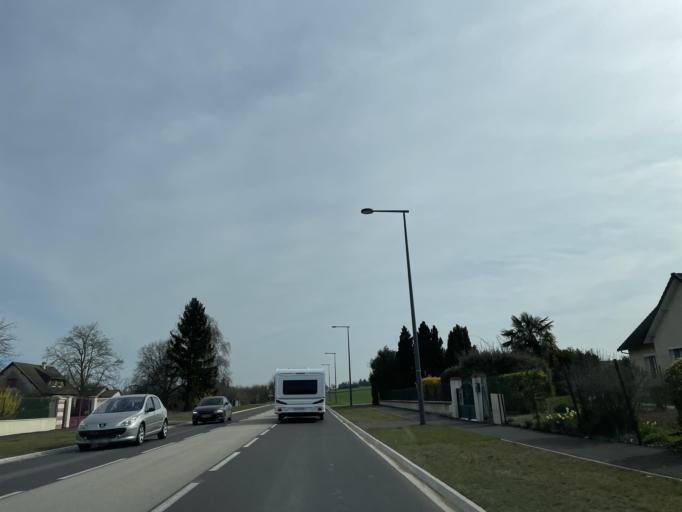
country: FR
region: Champagne-Ardenne
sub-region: Departement de l'Aube
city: Romilly-sur-Seine
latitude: 48.5146
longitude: 3.6415
